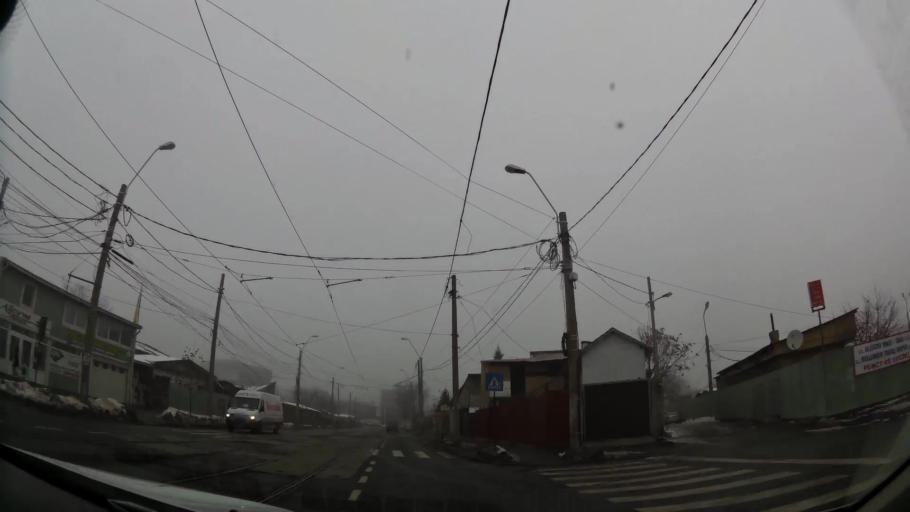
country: RO
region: Ilfov
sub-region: Comuna Chiajna
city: Rosu
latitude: 44.4700
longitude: 26.0235
